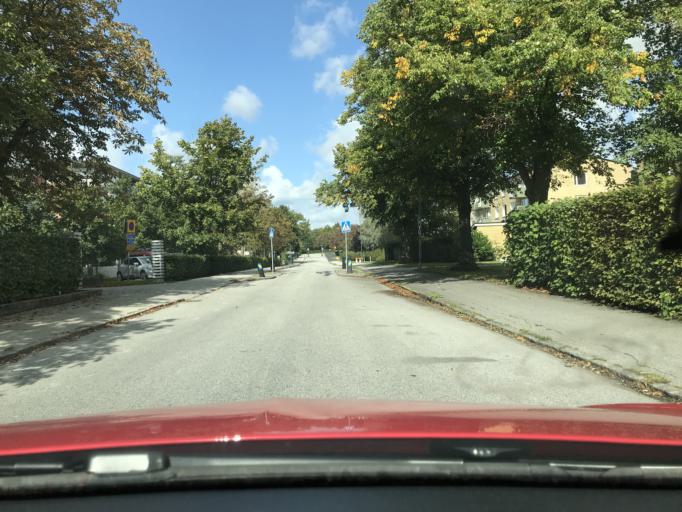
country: SE
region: Skane
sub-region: Lunds Kommun
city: Lund
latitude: 55.7181
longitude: 13.1949
